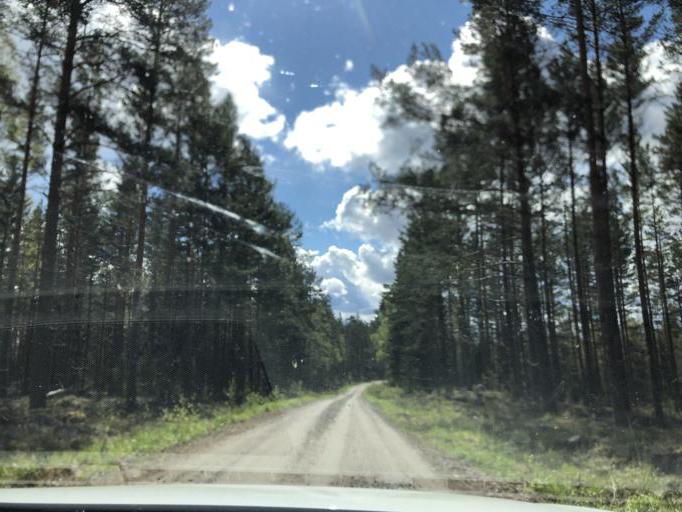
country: SE
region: Uppsala
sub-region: Heby Kommun
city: Tarnsjo
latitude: 60.2444
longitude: 16.9020
